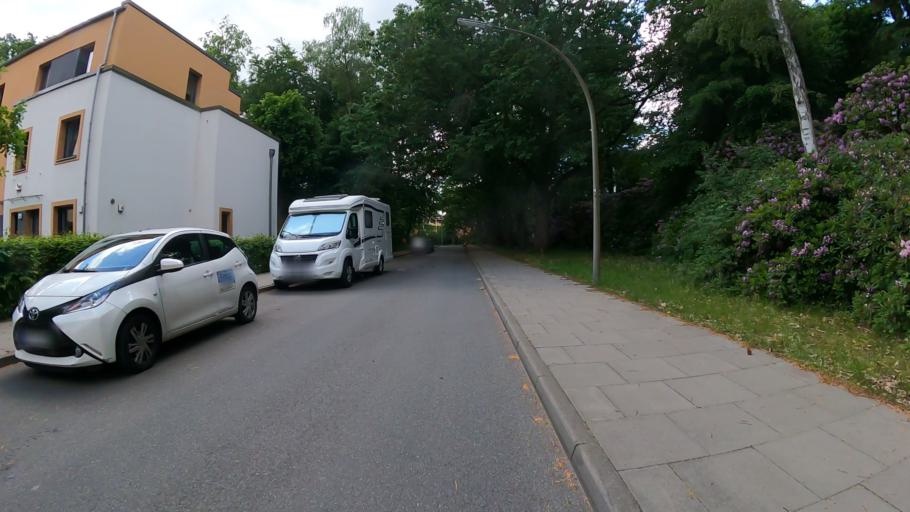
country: DE
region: Hamburg
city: Langenhorn
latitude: 53.6690
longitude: 10.0086
